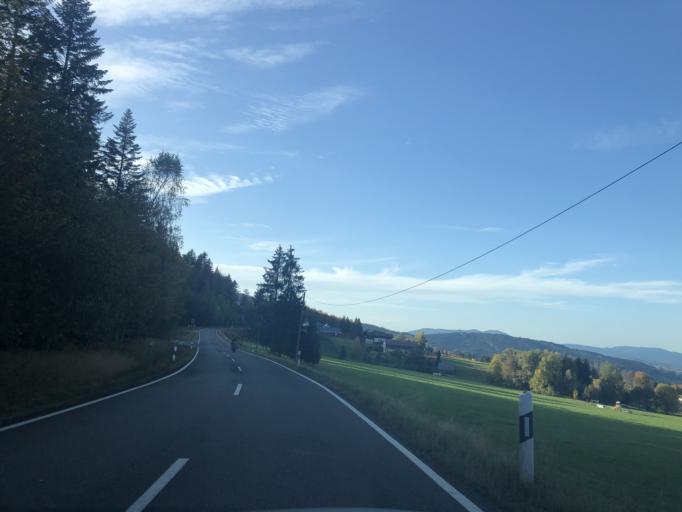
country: DE
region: Bavaria
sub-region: Lower Bavaria
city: Eppenschlag
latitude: 48.9370
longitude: 13.3160
